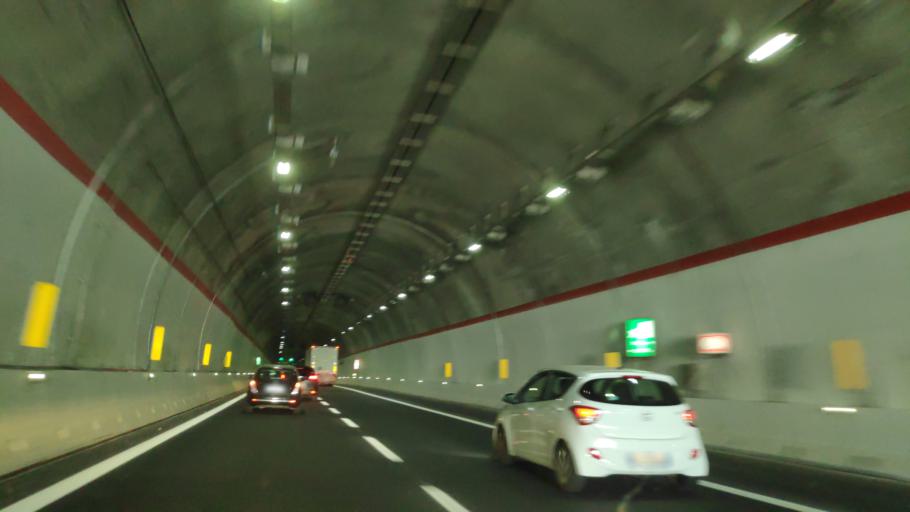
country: IT
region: Basilicate
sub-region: Provincia di Potenza
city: Lagonegro
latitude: 40.1399
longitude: 15.7578
